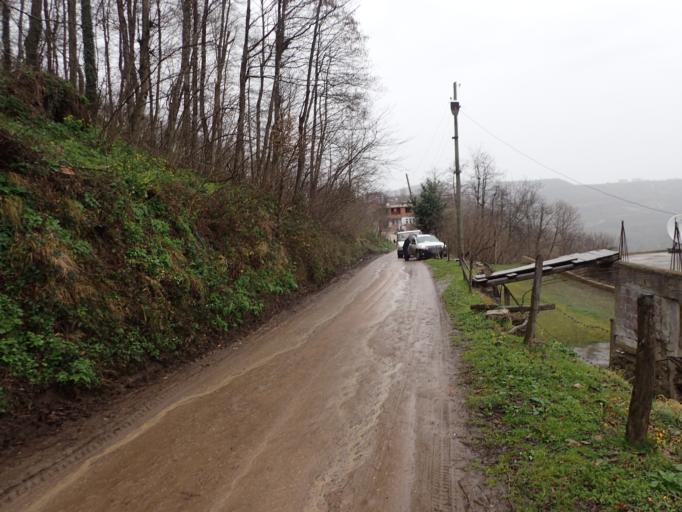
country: TR
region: Ordu
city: Camas
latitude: 40.8820
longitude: 37.4987
